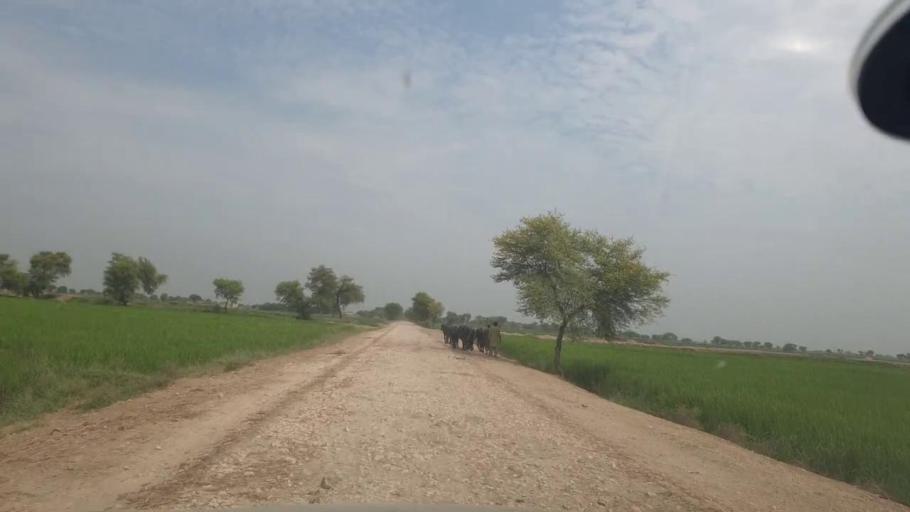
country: PK
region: Sindh
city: Jacobabad
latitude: 28.2464
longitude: 68.5418
